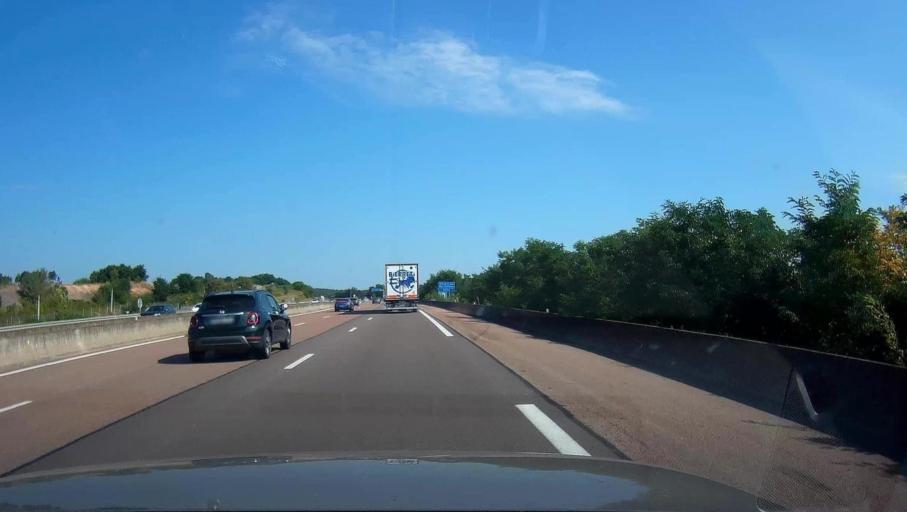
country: FR
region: Bourgogne
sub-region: Departement de la Cote-d'Or
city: Selongey
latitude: 47.5794
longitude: 5.2103
